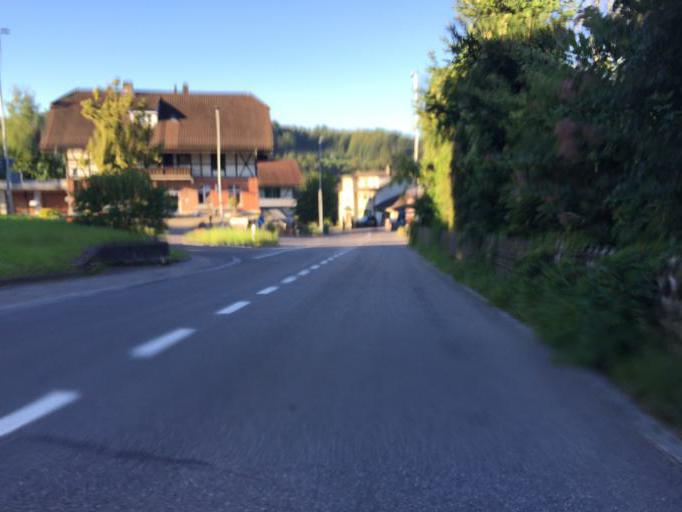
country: CH
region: Bern
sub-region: Bern-Mittelland District
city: Kirchlindach
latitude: 46.9753
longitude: 7.4232
